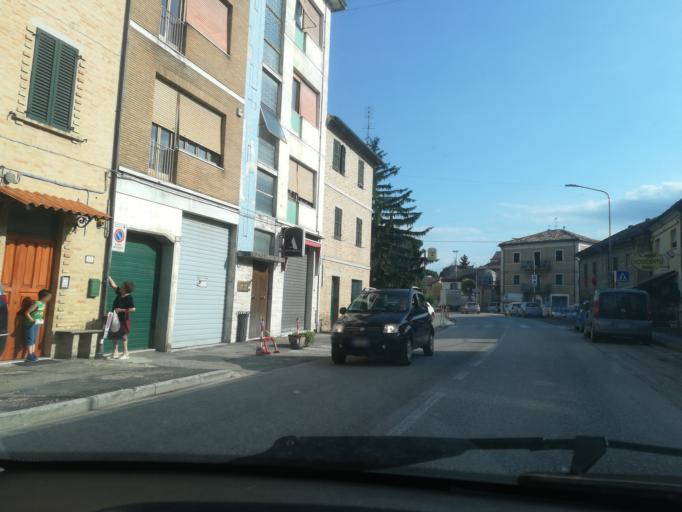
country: IT
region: The Marches
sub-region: Provincia di Macerata
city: Villa Potenza
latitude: 43.3246
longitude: 13.4261
